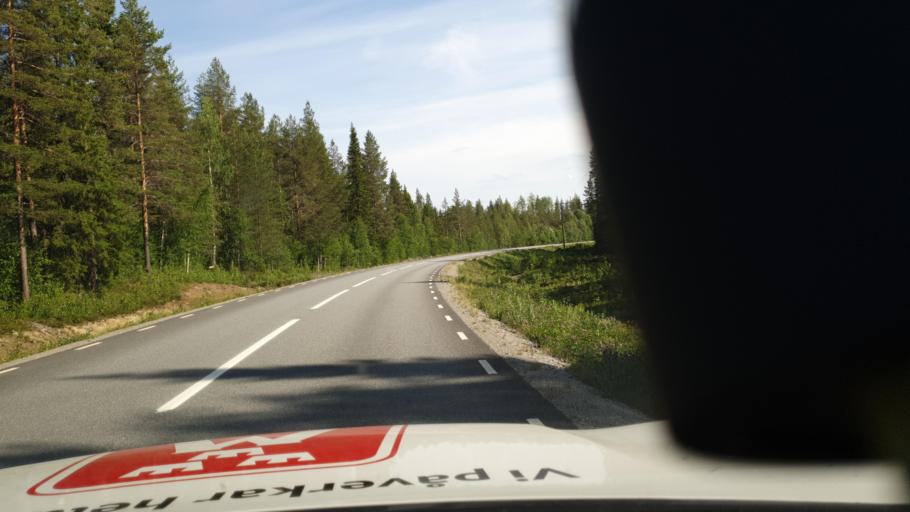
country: SE
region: Vaesterbotten
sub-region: Skelleftea Kommun
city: Langsele
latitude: 64.7509
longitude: 20.3467
